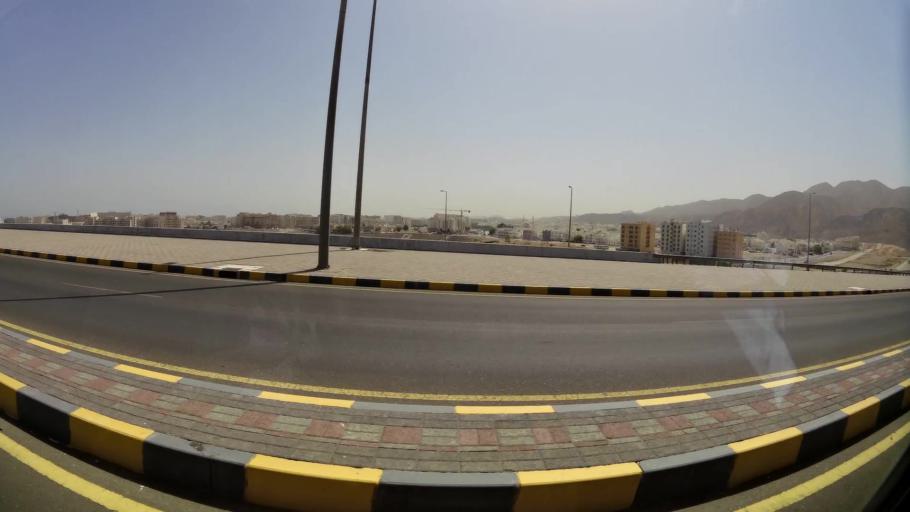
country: OM
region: Muhafazat Masqat
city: Bawshar
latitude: 23.5800
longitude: 58.4167
